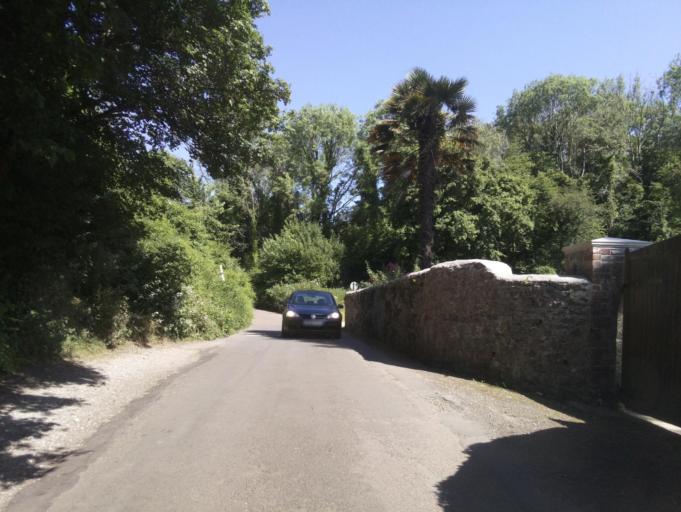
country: GB
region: England
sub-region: Borough of Torbay
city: Paignton
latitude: 50.4162
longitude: -3.6002
